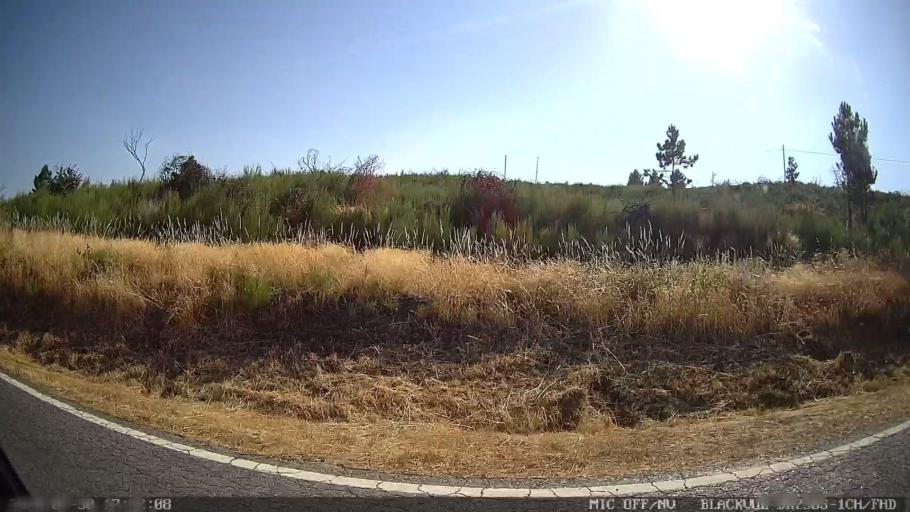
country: PT
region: Vila Real
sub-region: Sabrosa
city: Sabrosa
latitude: 41.3013
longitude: -7.4752
